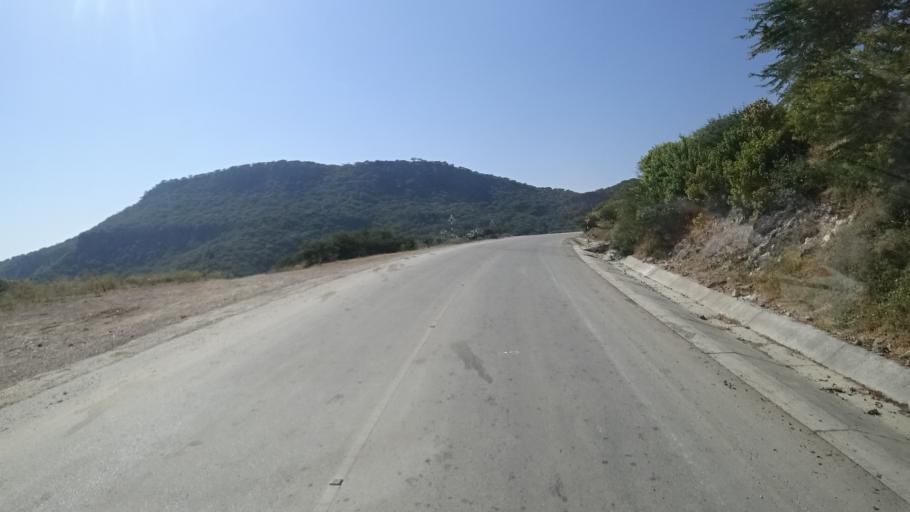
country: OM
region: Zufar
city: Salalah
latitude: 17.0572
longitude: 54.6114
